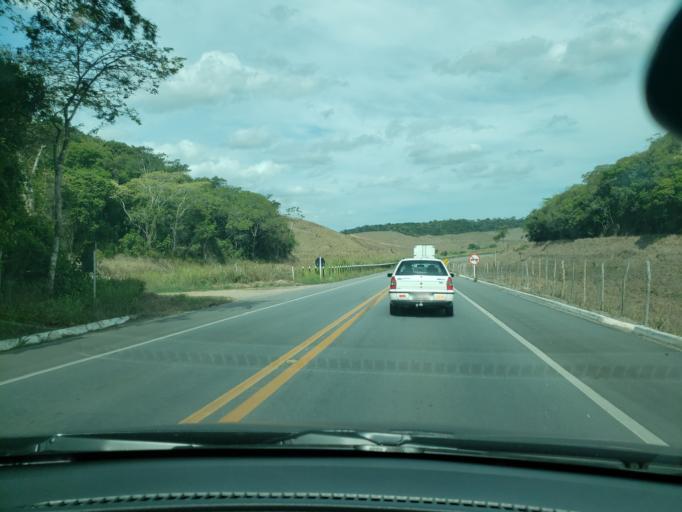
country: BR
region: Alagoas
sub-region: Murici
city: Murici
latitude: -9.3305
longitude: -35.9082
